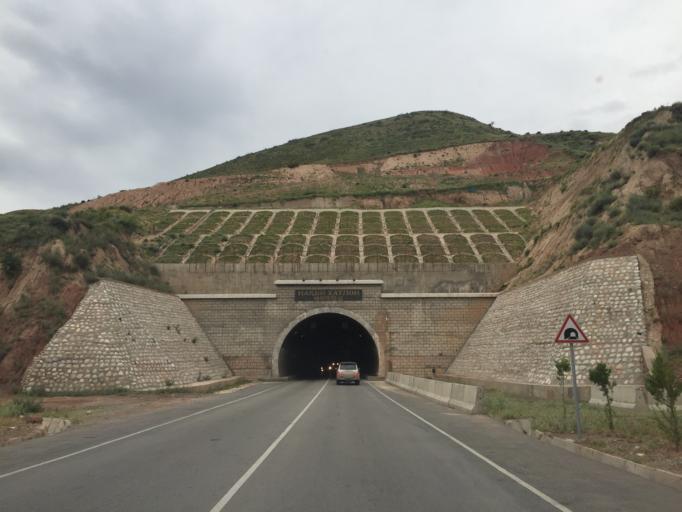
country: TJ
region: Khatlon
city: Norak
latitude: 38.4873
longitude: 69.1764
